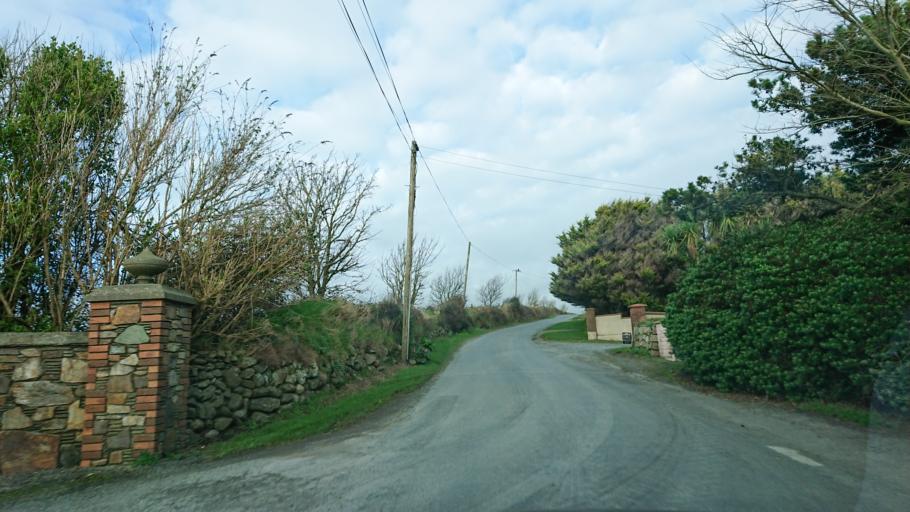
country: IE
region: Munster
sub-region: Waterford
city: Portlaw
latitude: 52.1405
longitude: -7.3059
